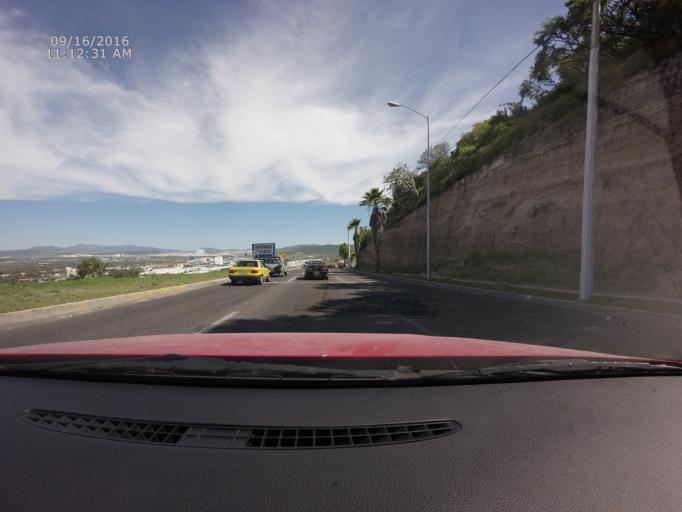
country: MX
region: Queretaro
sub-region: Queretaro
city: Sergio Villasenor
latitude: 20.6453
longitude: -100.4256
